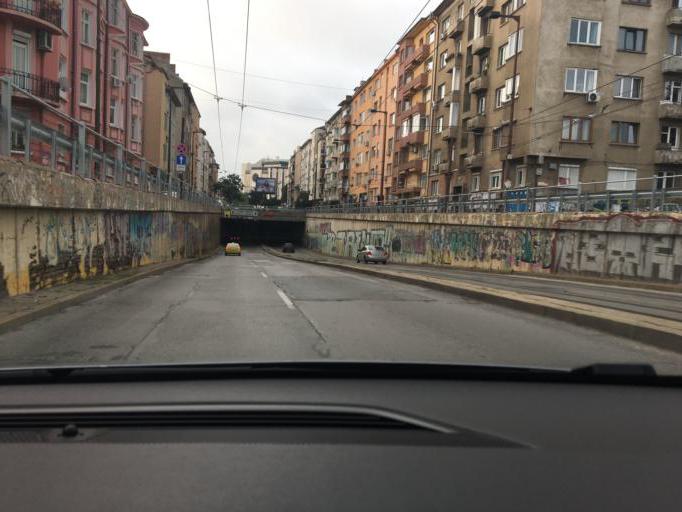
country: BG
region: Sofia-Capital
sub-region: Stolichna Obshtina
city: Sofia
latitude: 42.6880
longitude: 23.3159
